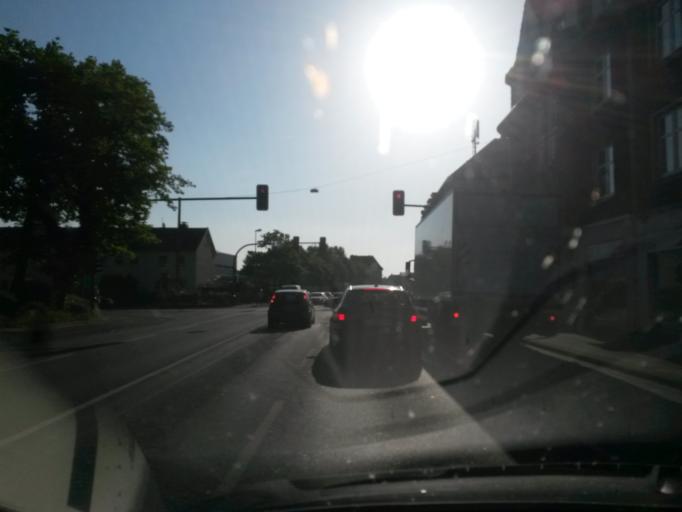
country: DE
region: North Rhine-Westphalia
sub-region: Regierungsbezirk Detmold
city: Bielefeld
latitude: 52.0220
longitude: 8.5526
